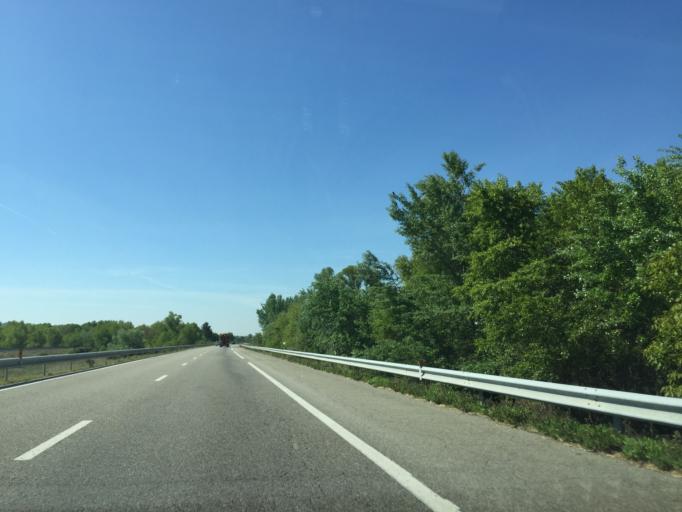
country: FR
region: Provence-Alpes-Cote d'Azur
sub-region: Departement des Alpes-de-Haute-Provence
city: Villeneuve
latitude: 43.8885
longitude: 5.8808
